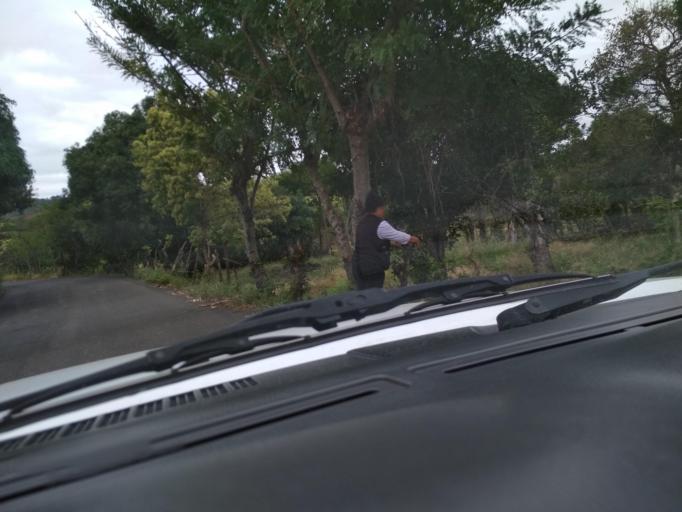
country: MX
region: Veracruz
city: Alto Lucero
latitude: 19.5951
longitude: -96.7845
